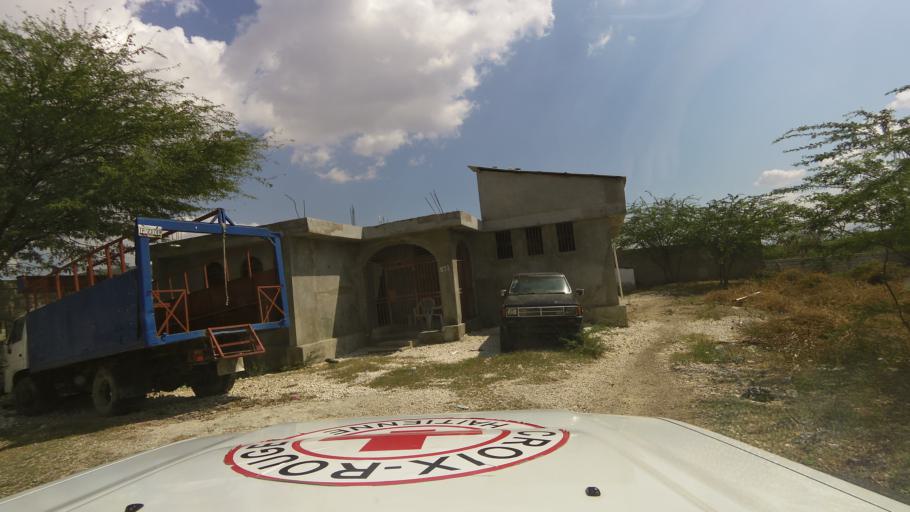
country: HT
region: Ouest
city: Croix des Bouquets
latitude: 18.6440
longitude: -72.2669
